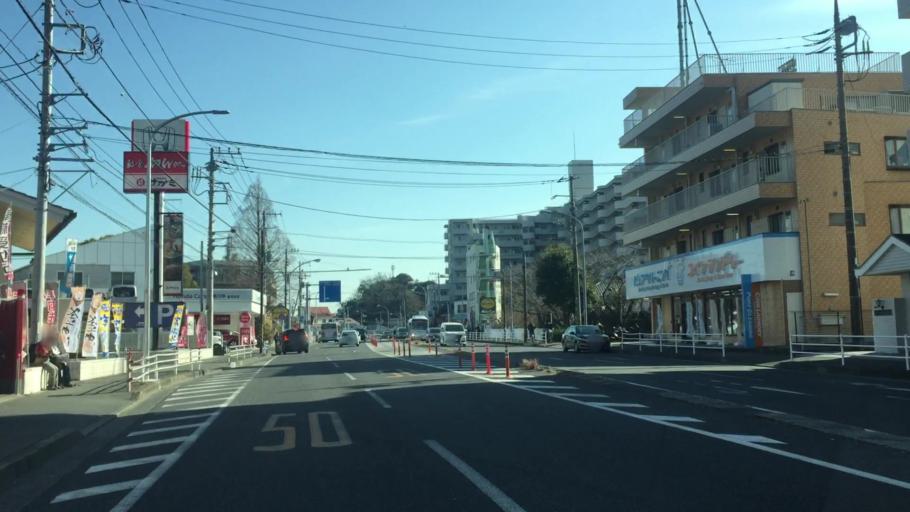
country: JP
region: Kanagawa
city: Zushi
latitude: 35.3463
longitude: 139.6092
